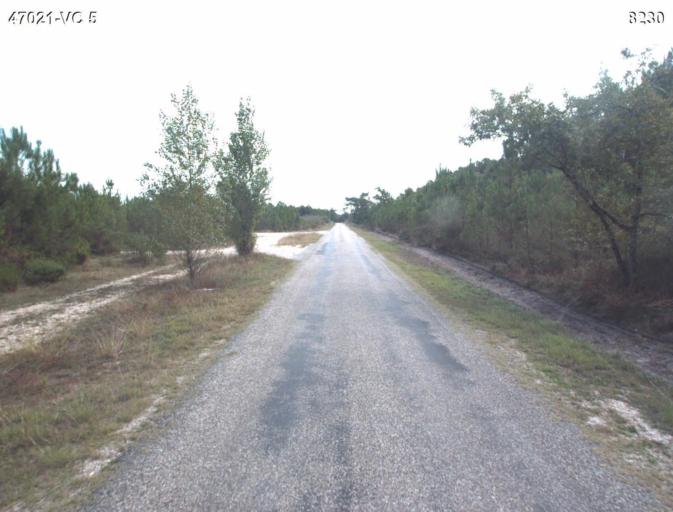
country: FR
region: Aquitaine
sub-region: Departement du Lot-et-Garonne
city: Barbaste
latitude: 44.1544
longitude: 0.1995
